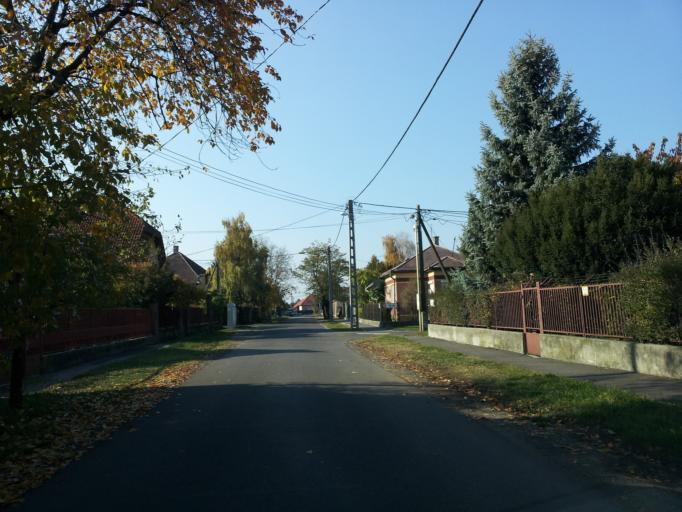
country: HU
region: Budapest
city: Budapest XVIII. keruelet
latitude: 47.4618
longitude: 19.1808
